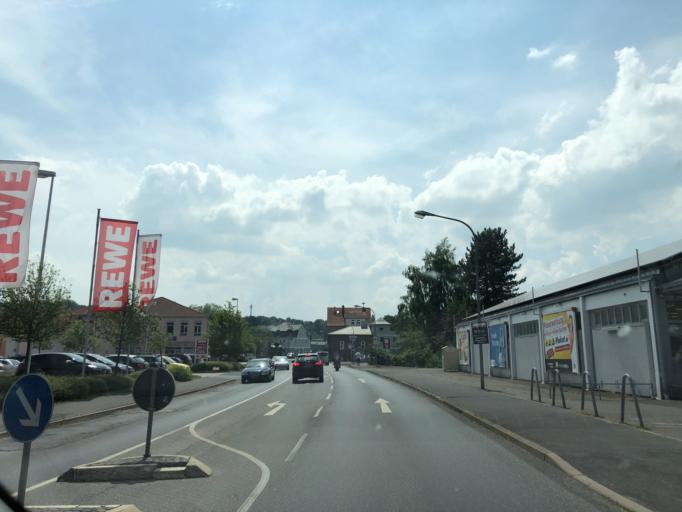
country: DE
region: Hesse
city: Schwalmstadt
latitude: 50.9138
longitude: 9.1819
